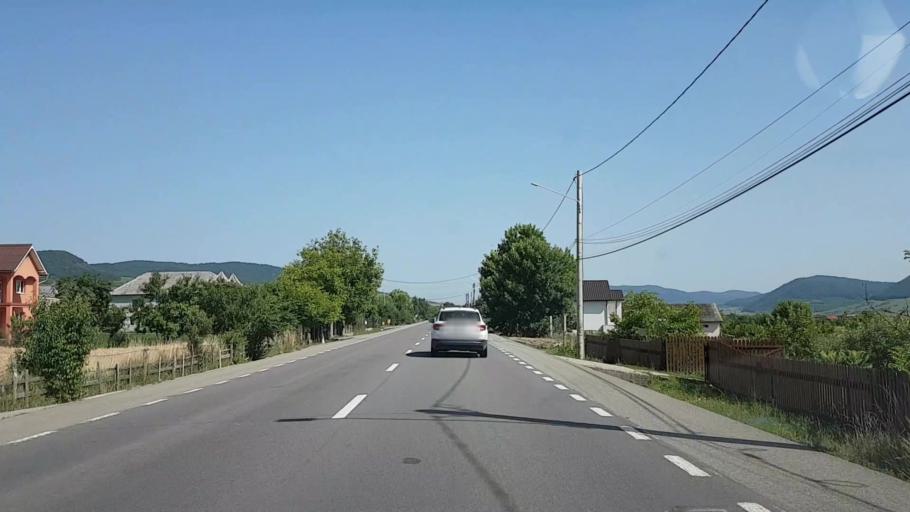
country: RO
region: Bistrita-Nasaud
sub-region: Comuna Sieu-Magherus
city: Sieu-Magherus
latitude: 47.0979
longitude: 24.3649
